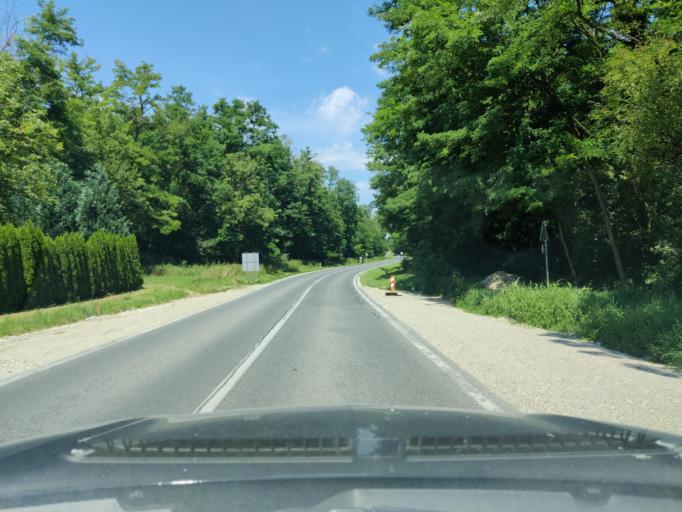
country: HR
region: Medimurska
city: Mackovec
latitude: 46.4534
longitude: 16.4316
